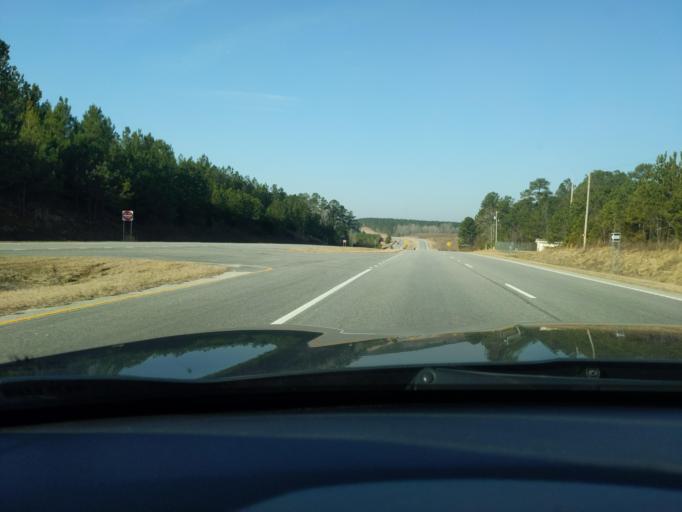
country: US
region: South Carolina
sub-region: Abbeville County
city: Abbeville
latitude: 34.1130
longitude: -82.4732
